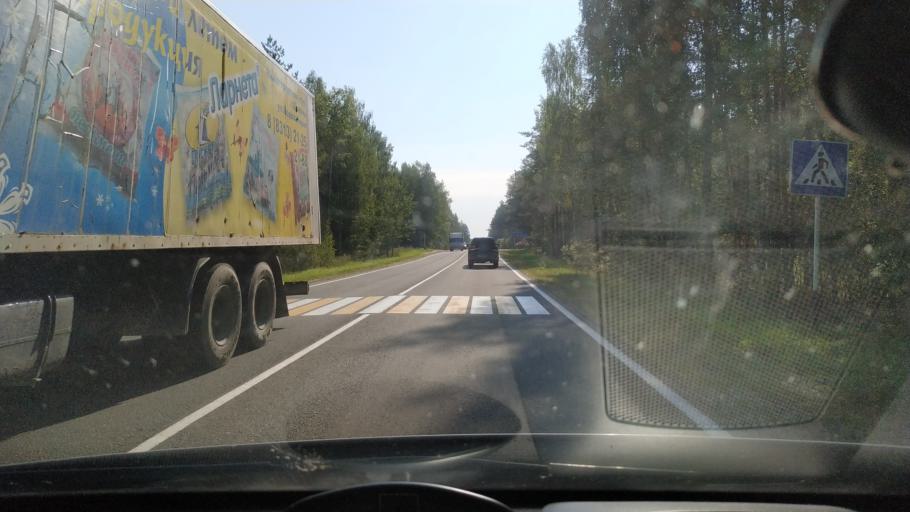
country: RU
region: Rjazan
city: Spas-Klepiki
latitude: 55.2244
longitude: 40.0688
